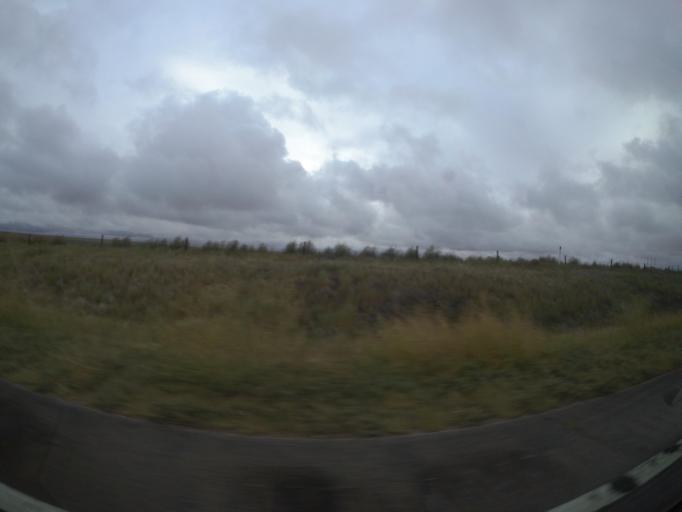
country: US
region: Colorado
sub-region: Washington County
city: Akron
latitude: 39.7391
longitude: -103.1761
